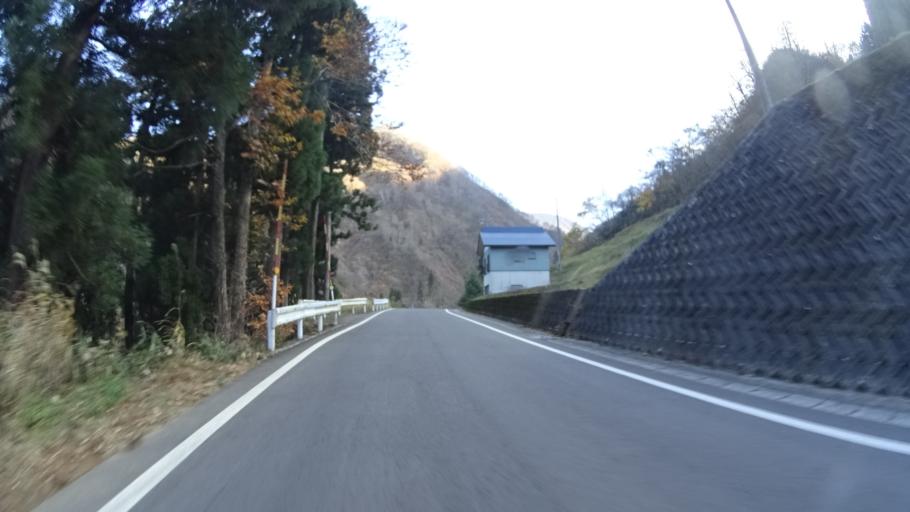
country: JP
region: Niigata
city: Shiozawa
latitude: 36.9757
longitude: 138.7480
